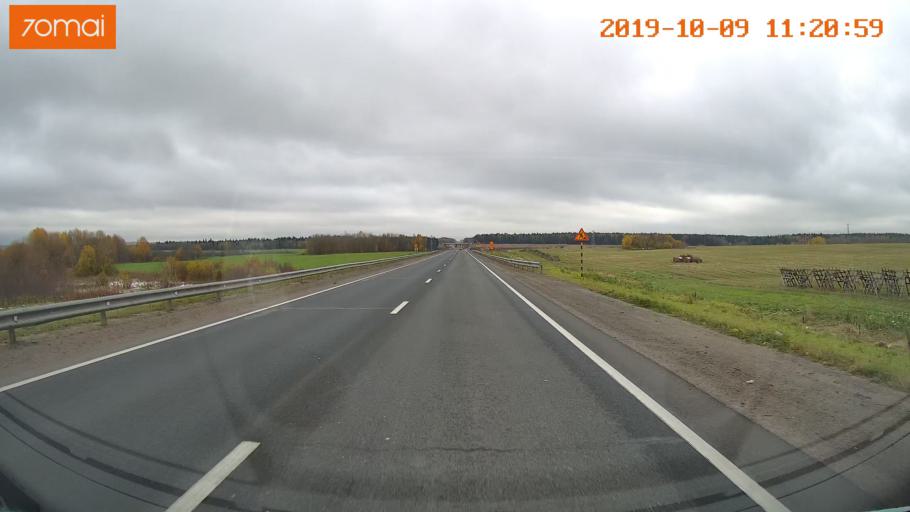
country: RU
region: Vologda
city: Vologda
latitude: 59.1436
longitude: 39.9451
